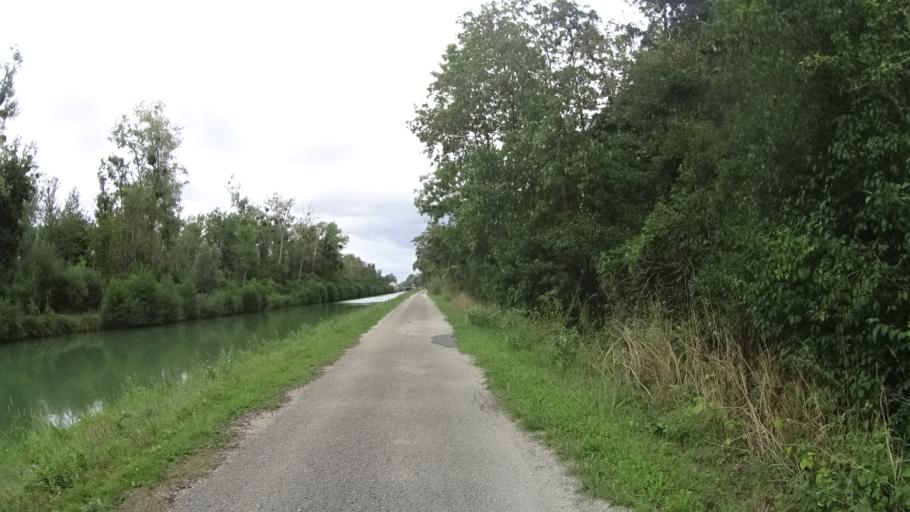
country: FR
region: Picardie
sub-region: Departement de l'Aisne
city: La Fere
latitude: 49.6739
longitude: 3.3579
